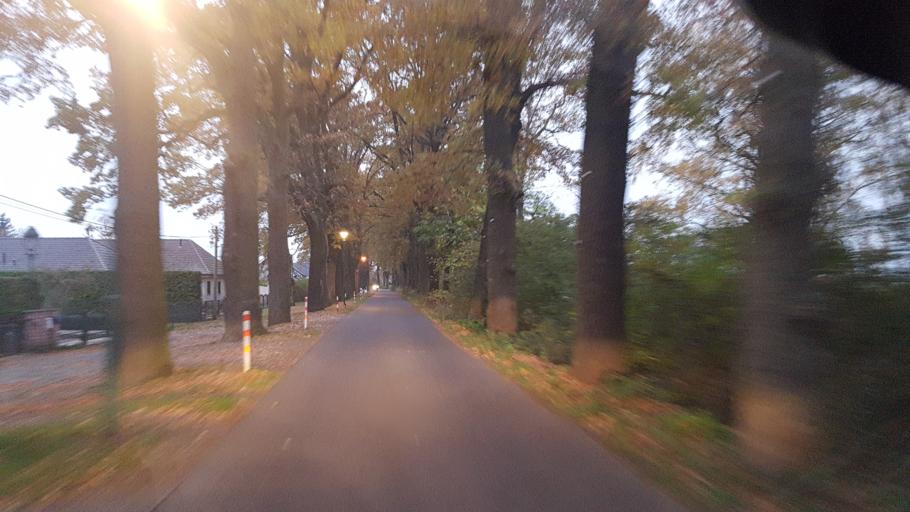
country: DE
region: Brandenburg
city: Nauen
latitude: 52.6368
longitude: 12.9070
